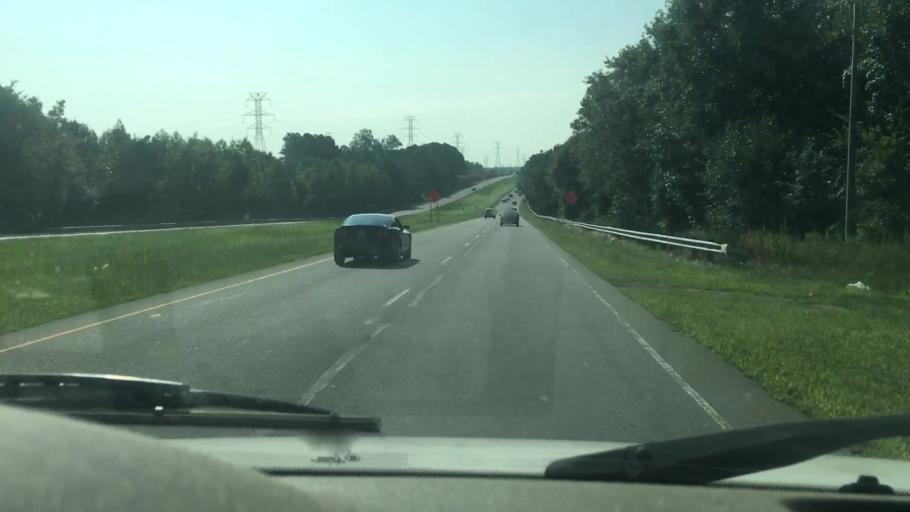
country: US
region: North Carolina
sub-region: Gaston County
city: Mount Holly
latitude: 35.3306
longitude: -80.9525
